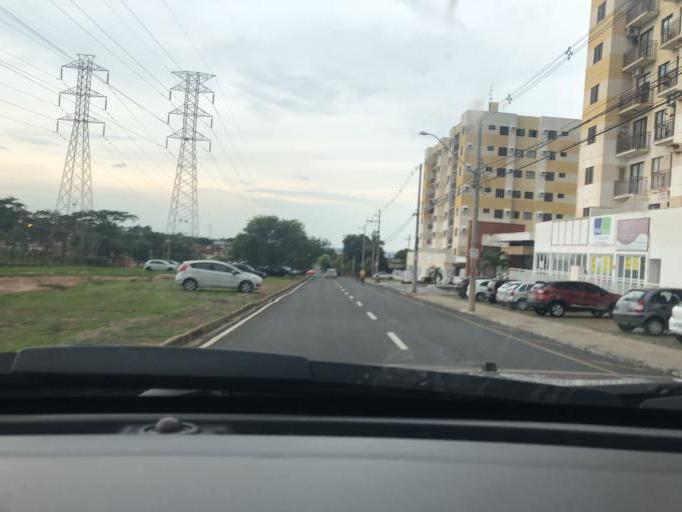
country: BR
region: Sao Paulo
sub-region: Sao Jose Do Rio Preto
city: Sao Jose do Rio Preto
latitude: -20.8444
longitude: -49.3867
